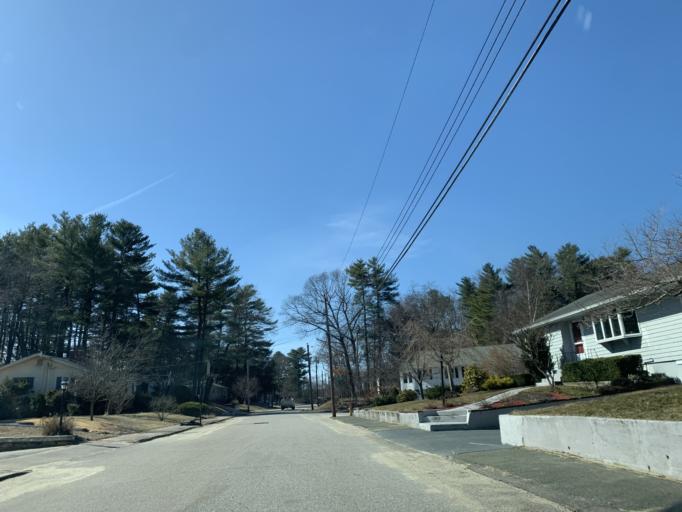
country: US
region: Massachusetts
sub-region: Norfolk County
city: Sharon
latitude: 42.1151
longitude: -71.1860
